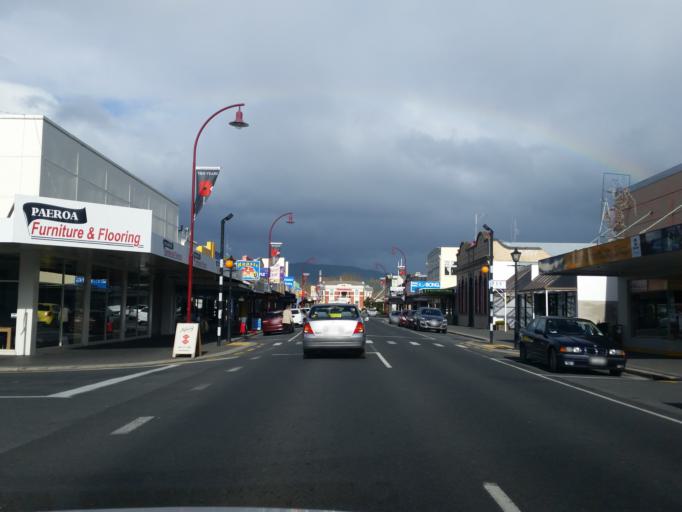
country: NZ
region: Waikato
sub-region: Hauraki District
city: Paeroa
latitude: -37.3789
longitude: 175.6692
